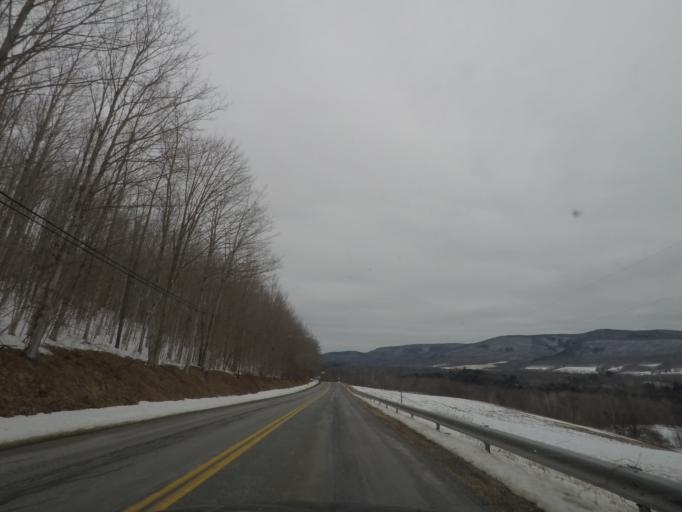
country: US
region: Massachusetts
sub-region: Berkshire County
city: Lanesborough
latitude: 42.5700
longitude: -73.3793
